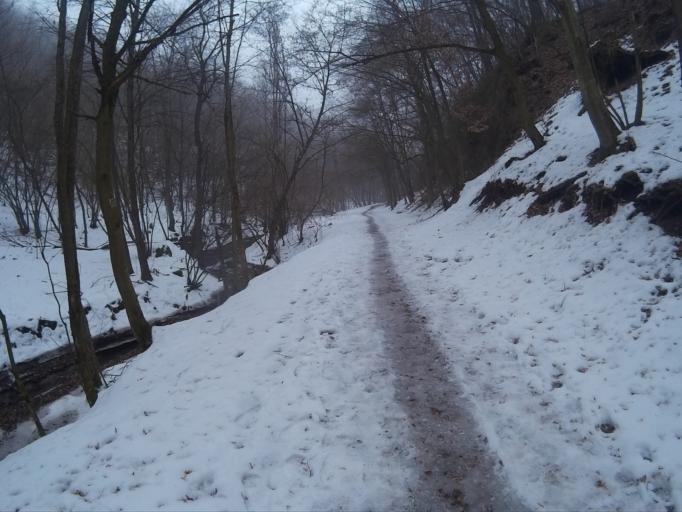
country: HU
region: Nograd
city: Matraverebely
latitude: 48.0013
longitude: 19.7591
